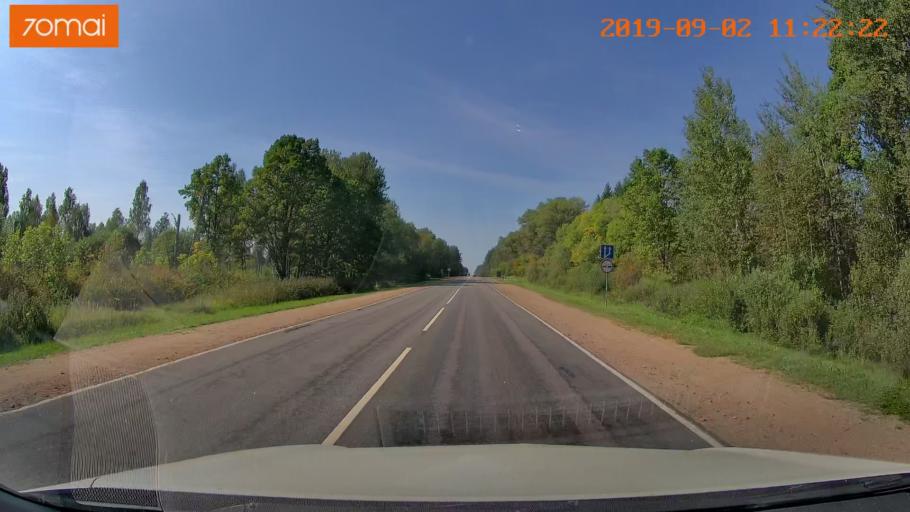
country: RU
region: Smolensk
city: Roslavl'
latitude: 54.0267
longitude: 33.0155
